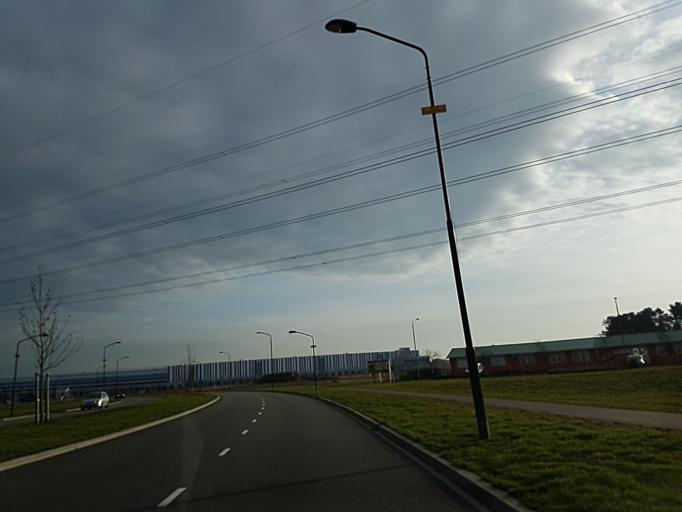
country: NL
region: North Brabant
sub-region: Roosendaal
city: Roosendaal
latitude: 51.5616
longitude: 4.4746
